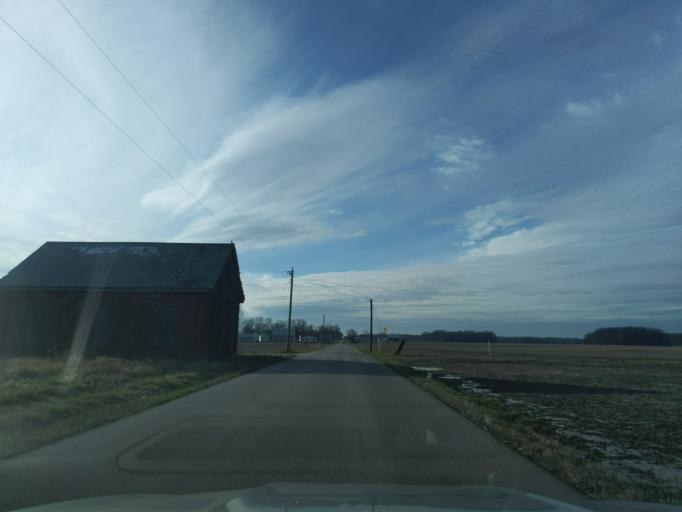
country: US
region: Indiana
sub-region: Decatur County
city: Westport
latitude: 39.1901
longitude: -85.4691
